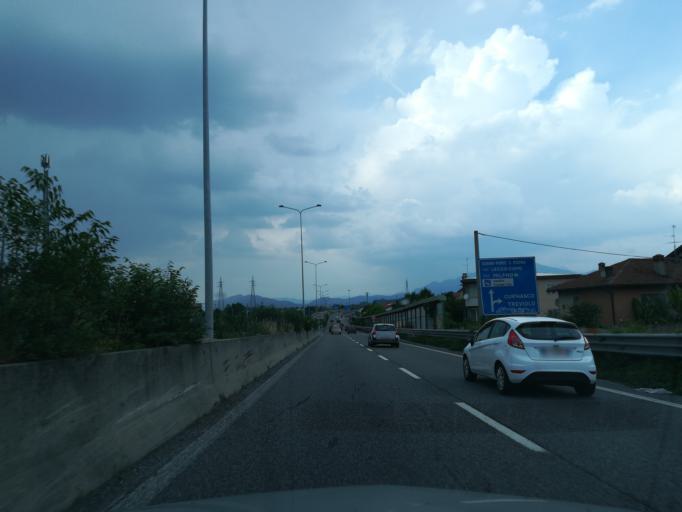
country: IT
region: Lombardy
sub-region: Provincia di Bergamo
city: Lallio
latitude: 45.6761
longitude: 9.6441
